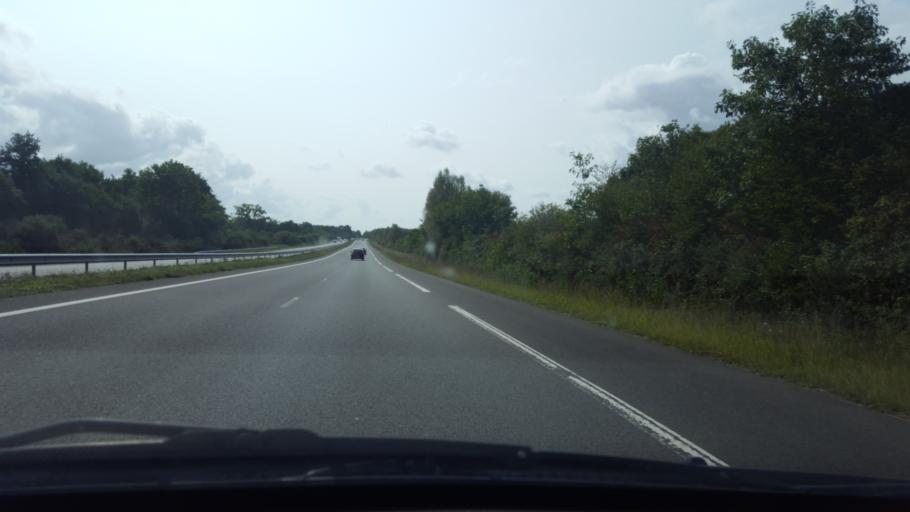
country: FR
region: Pays de la Loire
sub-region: Departement de la Loire-Atlantique
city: Saint-Lumine-de-Coutais
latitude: 47.0072
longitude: -1.7160
